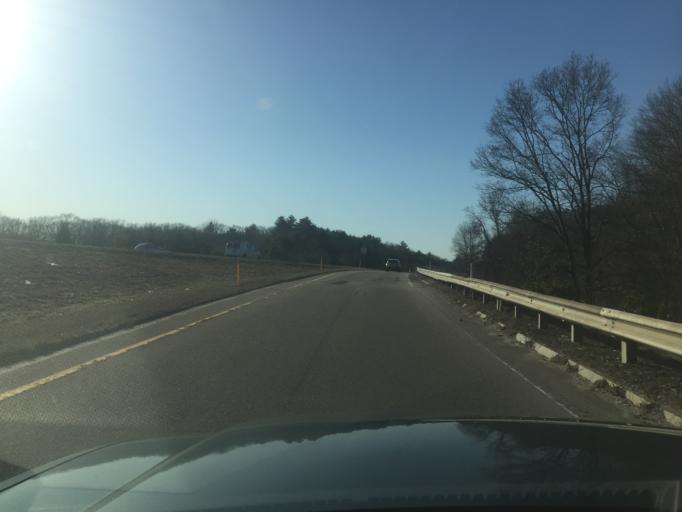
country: US
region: Massachusetts
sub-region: Norfolk County
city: Franklin
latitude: 42.0661
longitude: -71.4018
